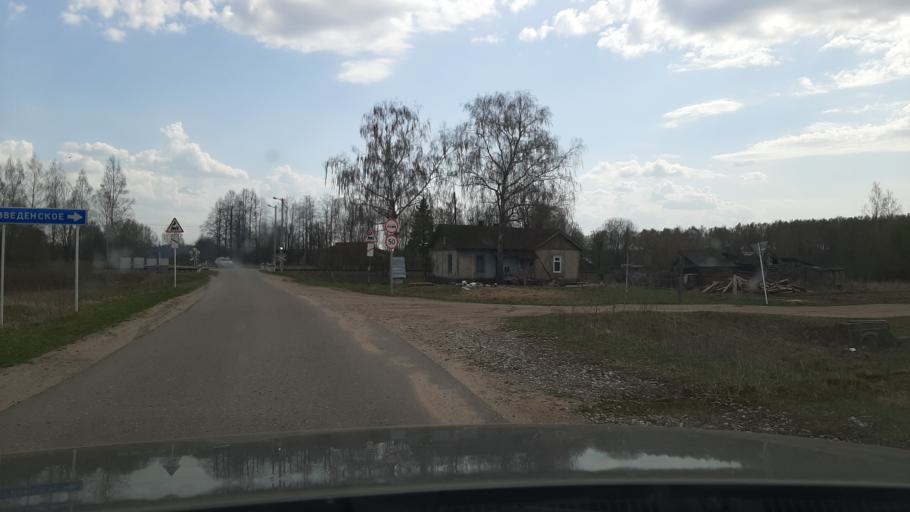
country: RU
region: Ivanovo
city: Furmanov
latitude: 57.3034
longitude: 41.1618
